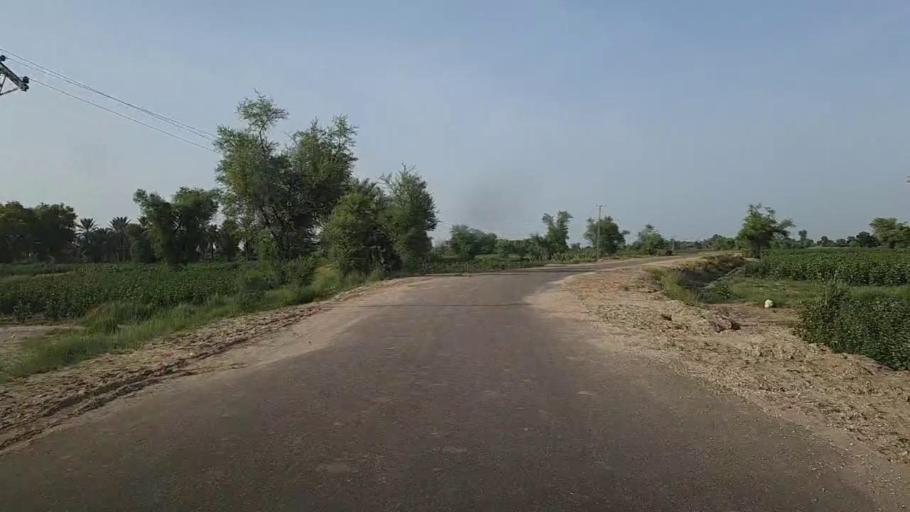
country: PK
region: Sindh
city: Ubauro
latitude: 28.1070
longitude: 69.8477
